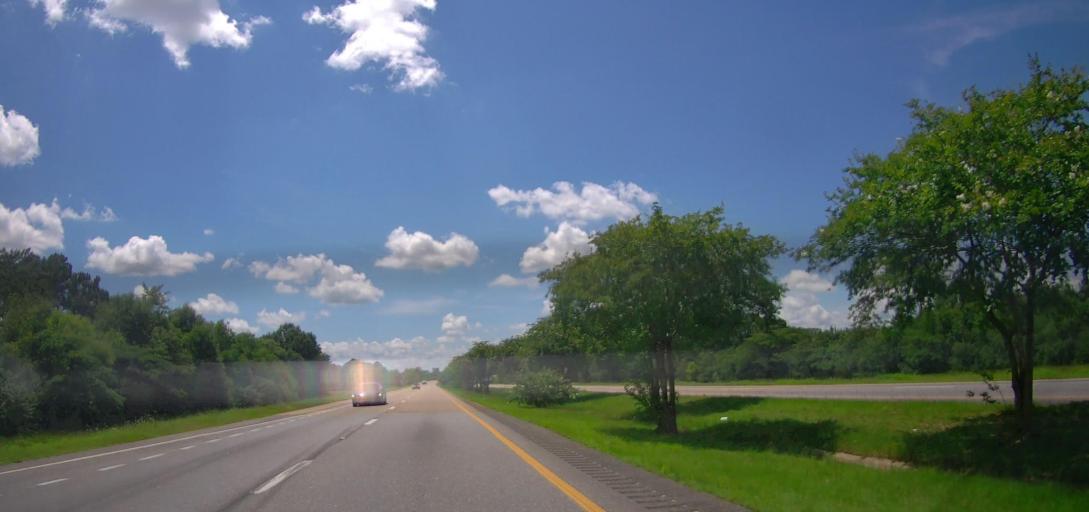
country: US
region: Alabama
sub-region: Montgomery County
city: Montgomery
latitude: 32.4226
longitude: -86.2718
